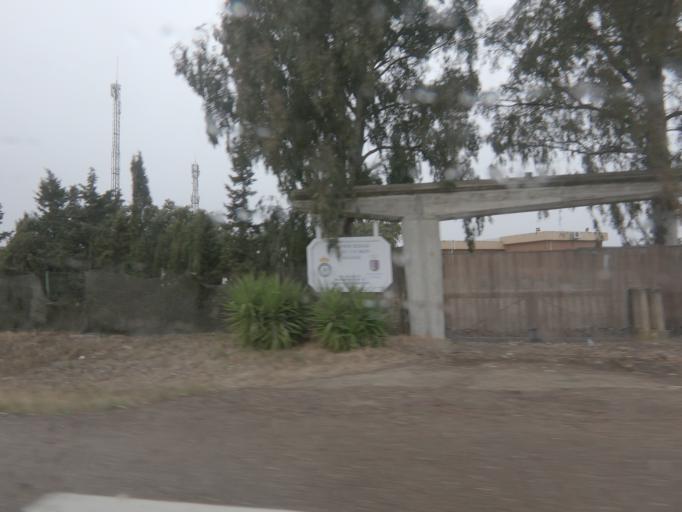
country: ES
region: Extremadura
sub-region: Provincia de Badajoz
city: Badajoz
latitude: 38.9472
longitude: -6.9152
